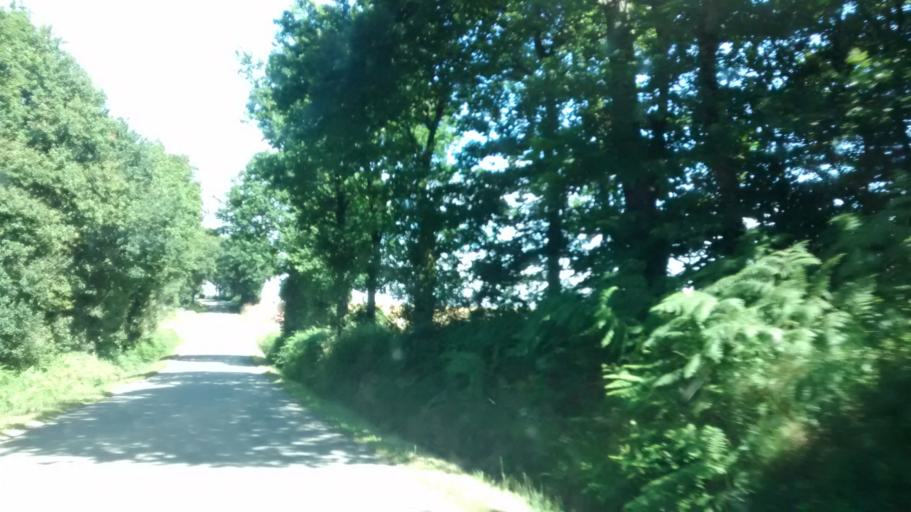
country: FR
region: Brittany
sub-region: Departement du Morbihan
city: Campeneac
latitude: 47.9922
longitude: -2.3062
